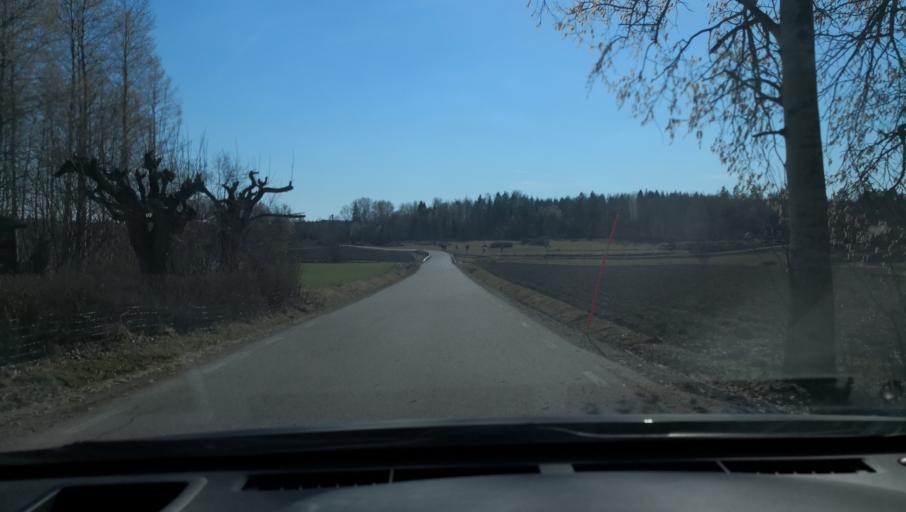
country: SE
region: Vaestmanland
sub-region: Sala Kommun
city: Sala
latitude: 60.0841
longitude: 16.5004
